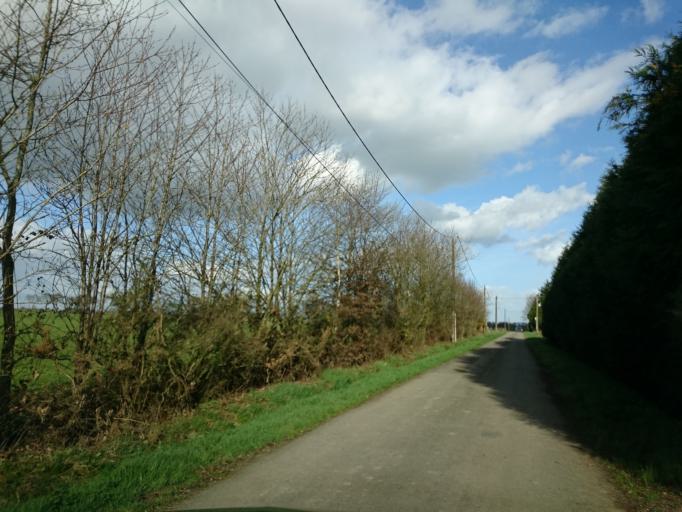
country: FR
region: Brittany
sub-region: Departement d'Ille-et-Vilaine
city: Crevin
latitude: 47.9285
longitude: -1.6477
